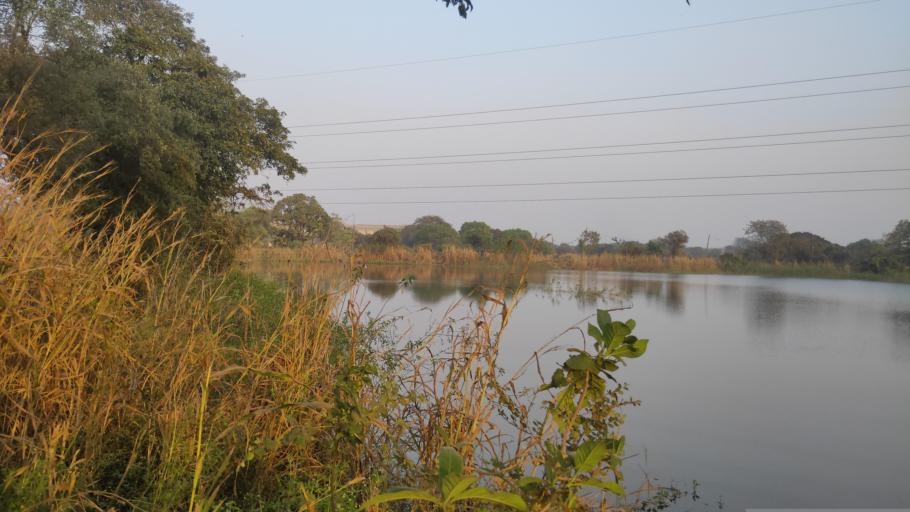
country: IN
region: Maharashtra
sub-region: Thane
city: Kalyan
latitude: 19.3016
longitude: 73.1405
